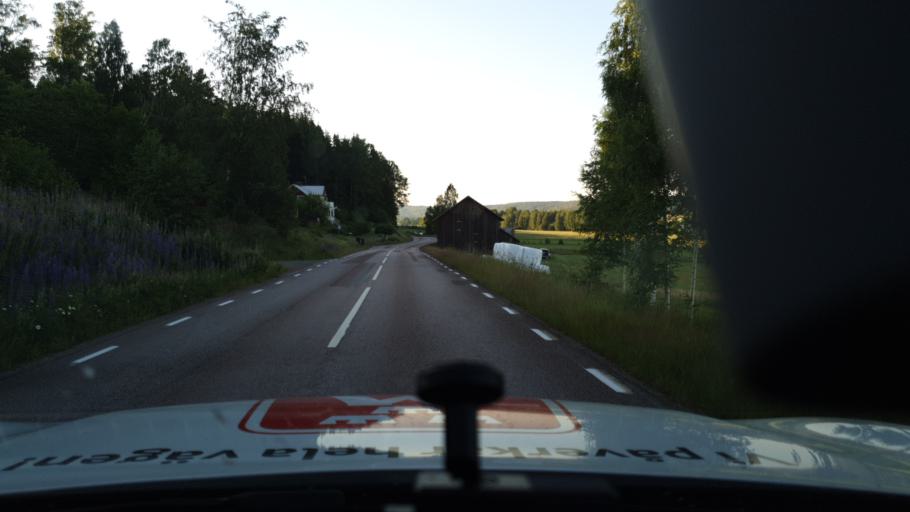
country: SE
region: Vaermland
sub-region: Kils Kommun
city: Kil
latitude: 59.5939
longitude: 13.3142
